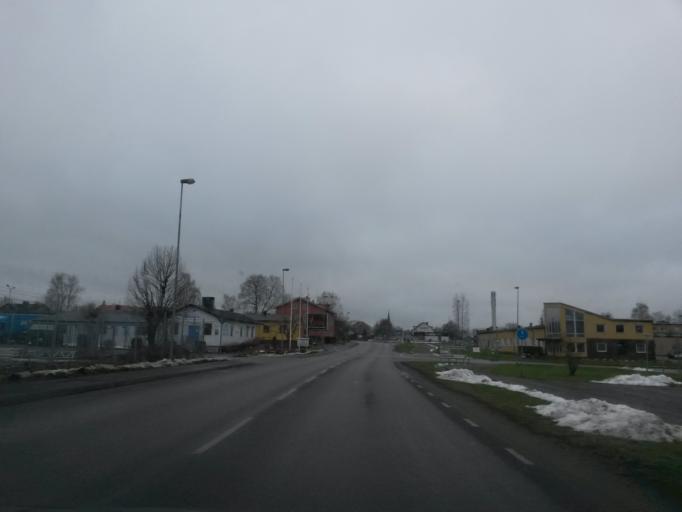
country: SE
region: Vaestra Goetaland
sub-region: Marks Kommun
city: Kinna
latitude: 57.5125
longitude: 12.7084
